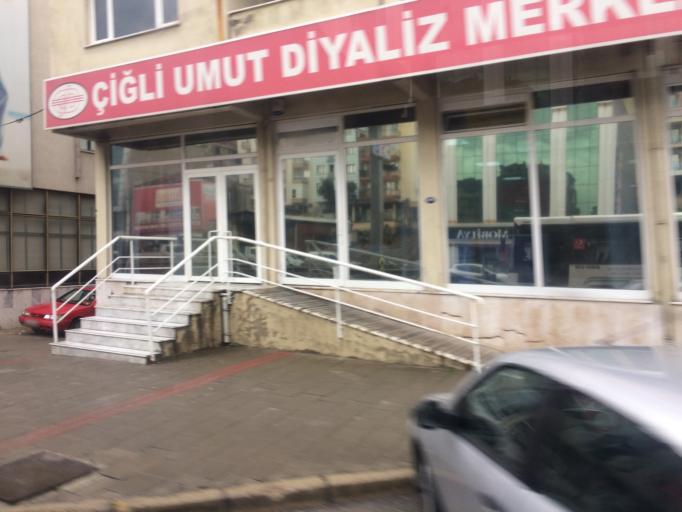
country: TR
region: Izmir
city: Karsiyaka
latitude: 38.4977
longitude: 27.0579
